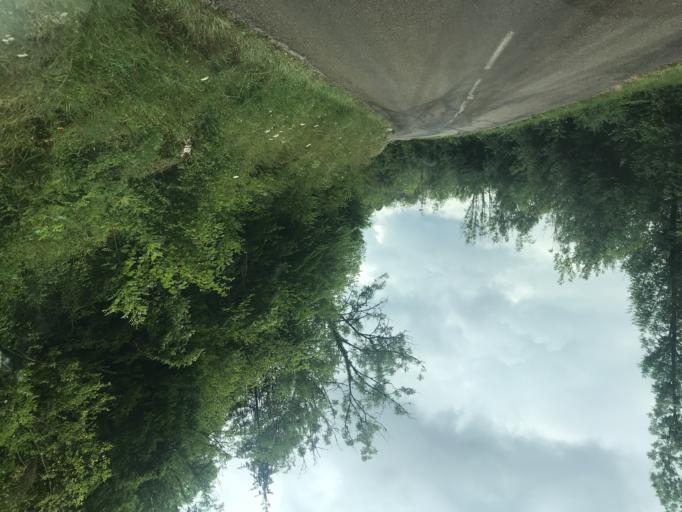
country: FR
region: Franche-Comte
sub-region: Departement du Jura
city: Saint-Claude
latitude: 46.3586
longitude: 5.8477
